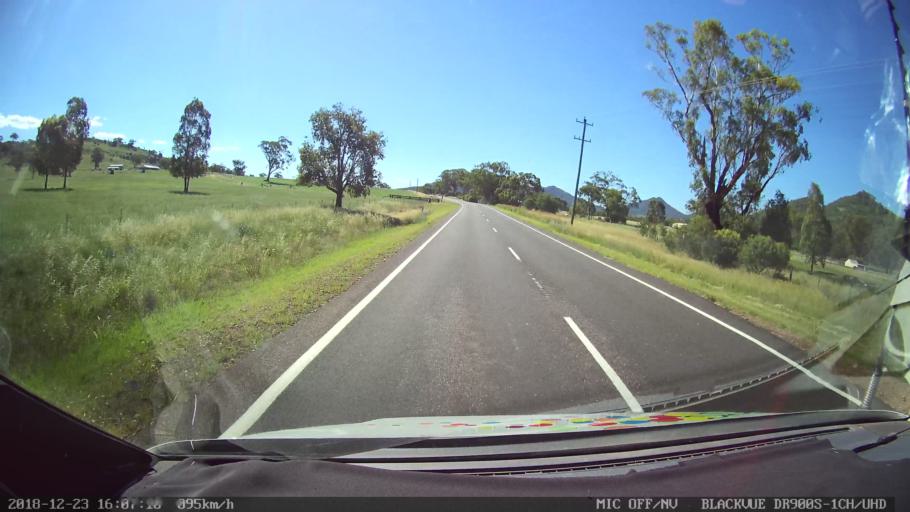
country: AU
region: New South Wales
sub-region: Tamworth Municipality
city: Phillip
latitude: -31.2735
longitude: 150.7658
